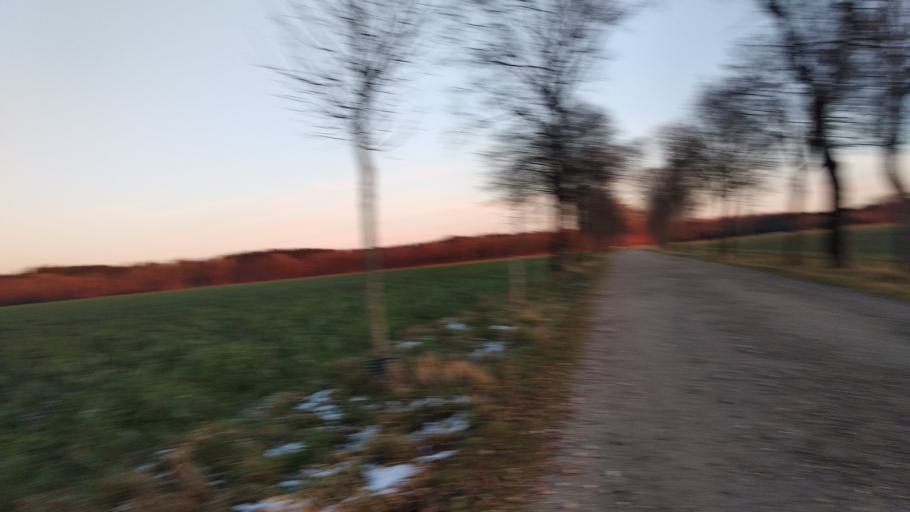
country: DE
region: Bavaria
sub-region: Upper Bavaria
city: Grasbrunn
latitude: 48.0713
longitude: 11.7781
